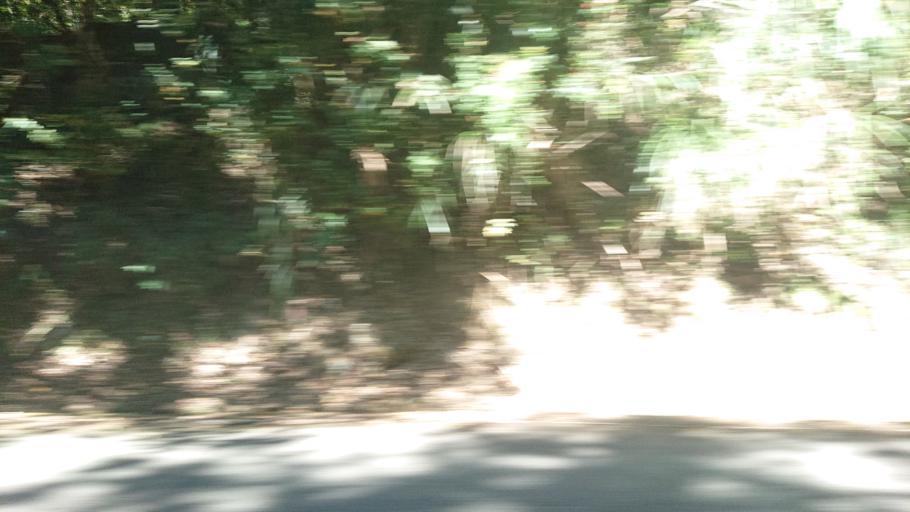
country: TW
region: Taiwan
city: Lugu
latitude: 23.4849
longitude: 120.8540
